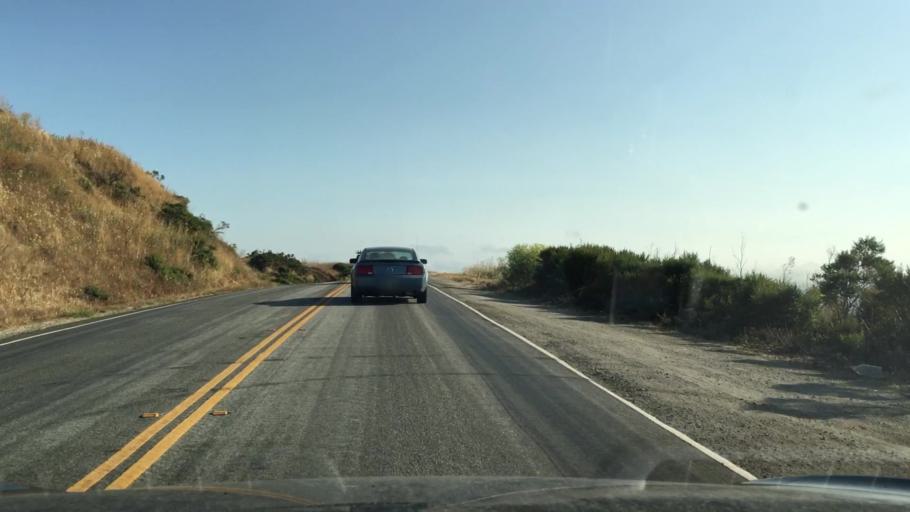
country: US
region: California
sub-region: San Mateo County
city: Portola Valley
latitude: 37.3660
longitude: -122.2478
